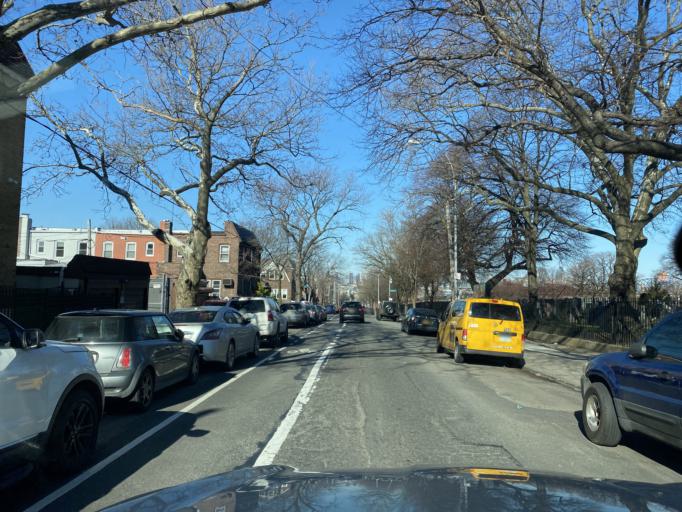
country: US
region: New York
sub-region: Queens County
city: Long Island City
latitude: 40.7101
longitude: -73.9145
